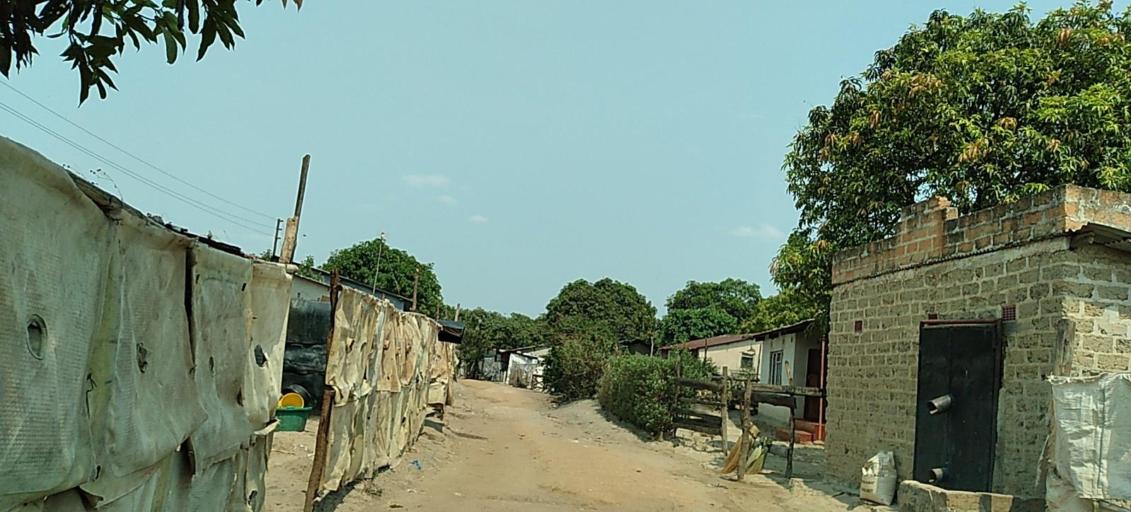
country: ZM
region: Copperbelt
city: Chambishi
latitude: -12.6311
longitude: 28.0732
